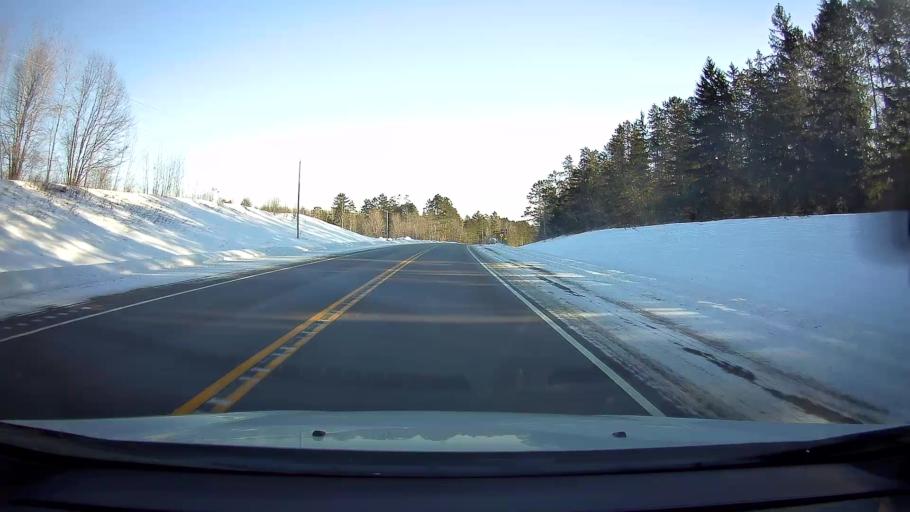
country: US
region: Wisconsin
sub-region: Sawyer County
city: Hayward
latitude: 46.0728
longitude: -91.4241
